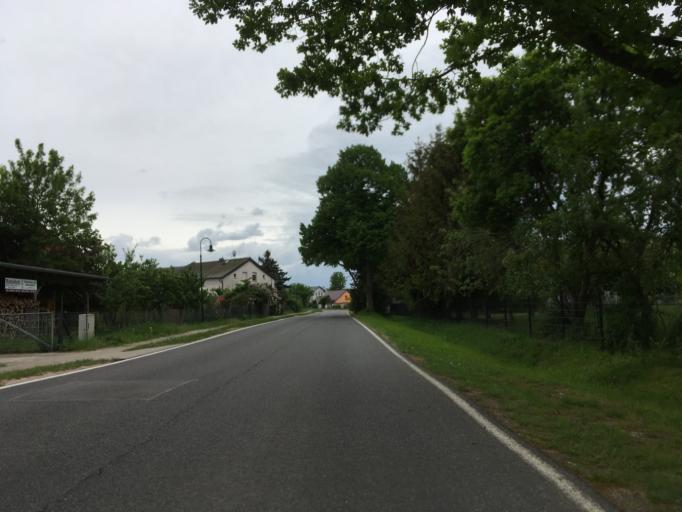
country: DE
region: Brandenburg
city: Werneuchen
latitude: 52.6652
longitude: 13.6903
